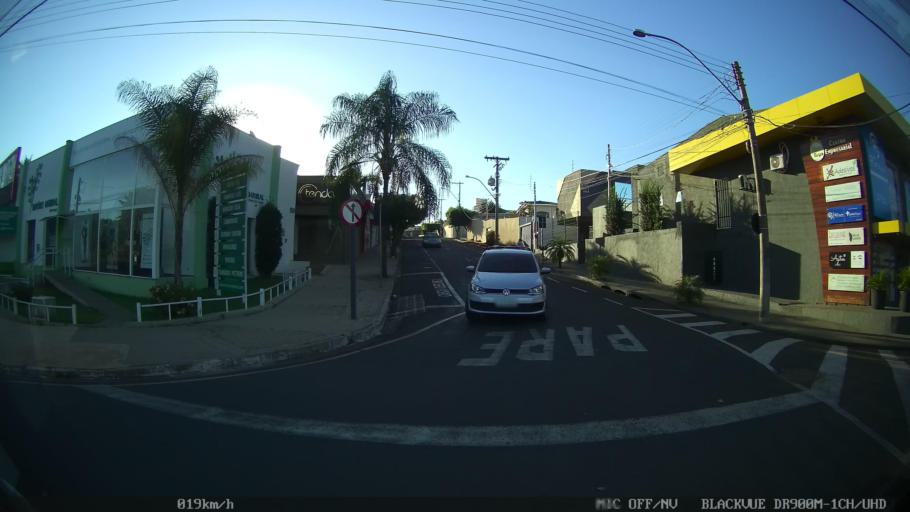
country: BR
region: Sao Paulo
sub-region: Sao Jose Do Rio Preto
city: Sao Jose do Rio Preto
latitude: -20.8080
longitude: -49.3672
